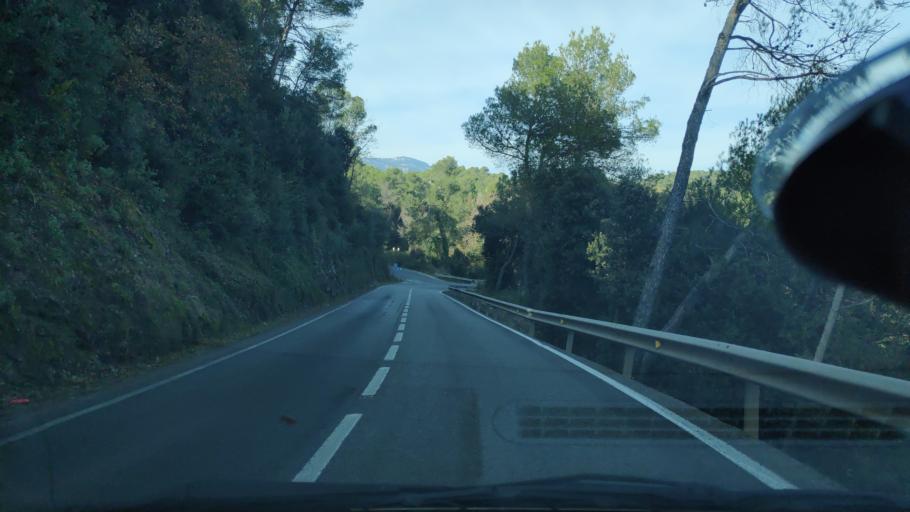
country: ES
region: Catalonia
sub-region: Provincia de Barcelona
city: Castellar del Valles
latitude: 41.6078
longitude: 2.0621
